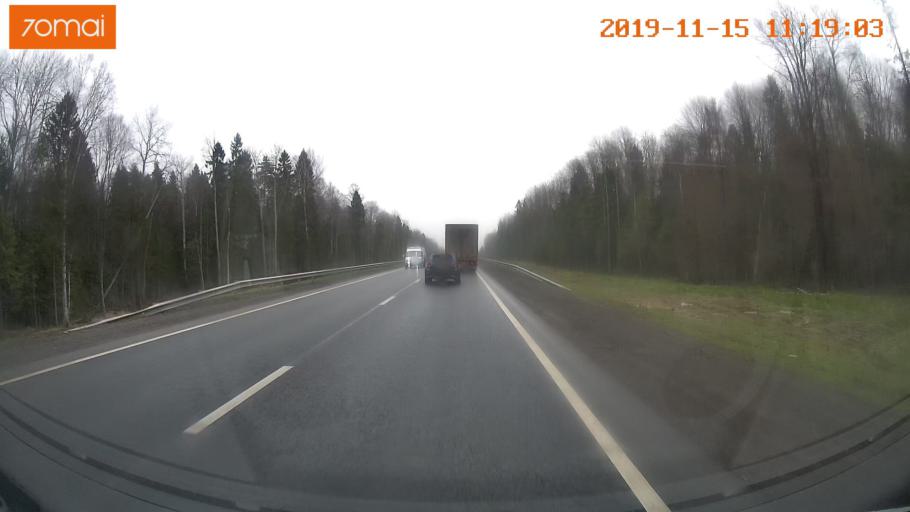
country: RU
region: Vologda
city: Molochnoye
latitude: 59.1374
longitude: 39.2842
